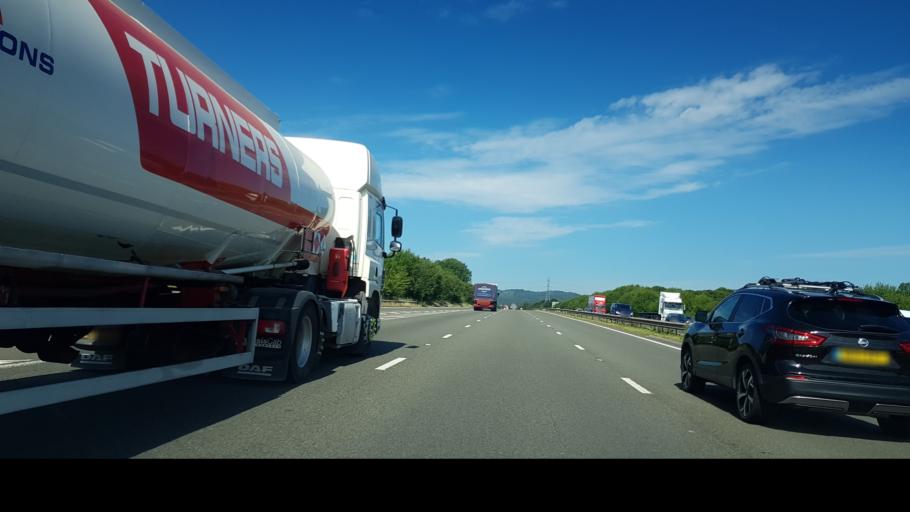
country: GB
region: Wales
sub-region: Caerphilly County Borough
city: Machen
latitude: 51.5421
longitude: -3.1322
